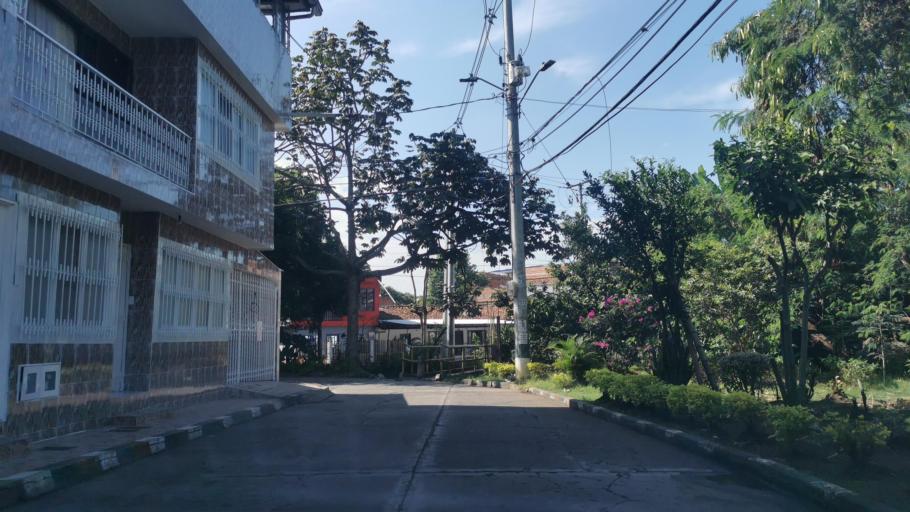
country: CO
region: Valle del Cauca
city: Jamundi
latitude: 3.2704
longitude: -76.5357
